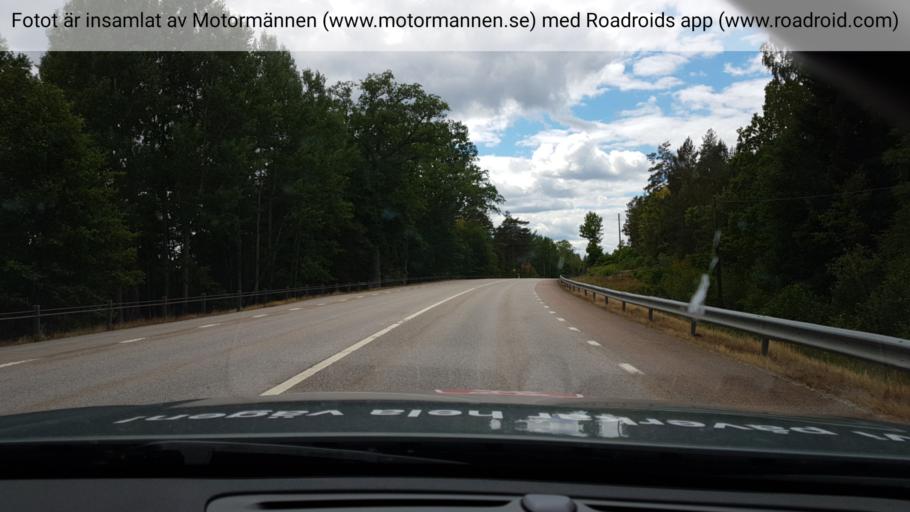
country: SE
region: Kalmar
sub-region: Oskarshamns Kommun
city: Oskarshamn
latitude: 57.4438
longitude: 16.4981
